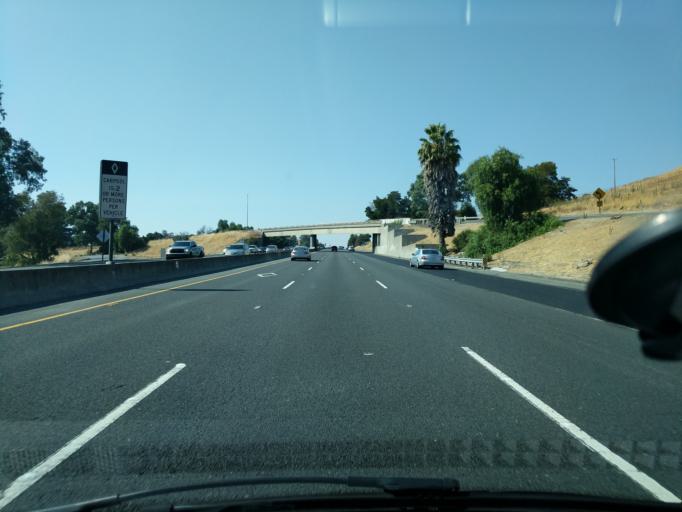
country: US
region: California
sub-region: Contra Costa County
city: Vine Hill
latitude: 38.0068
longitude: -122.0839
